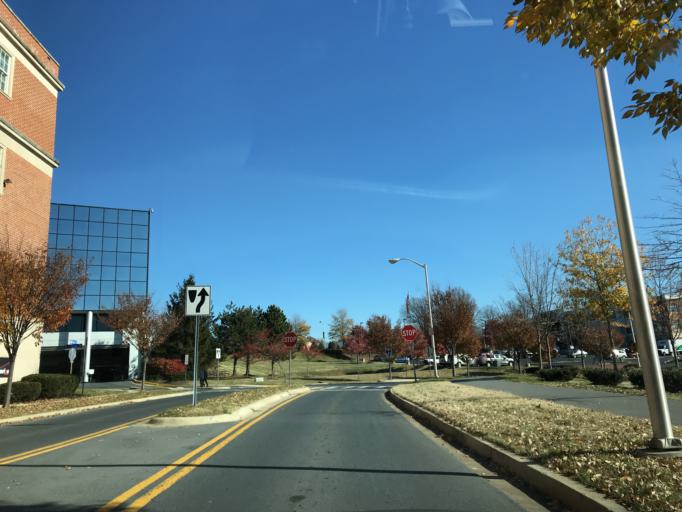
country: US
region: Maryland
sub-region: Montgomery County
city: Rockville
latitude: 39.0803
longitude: -77.1466
